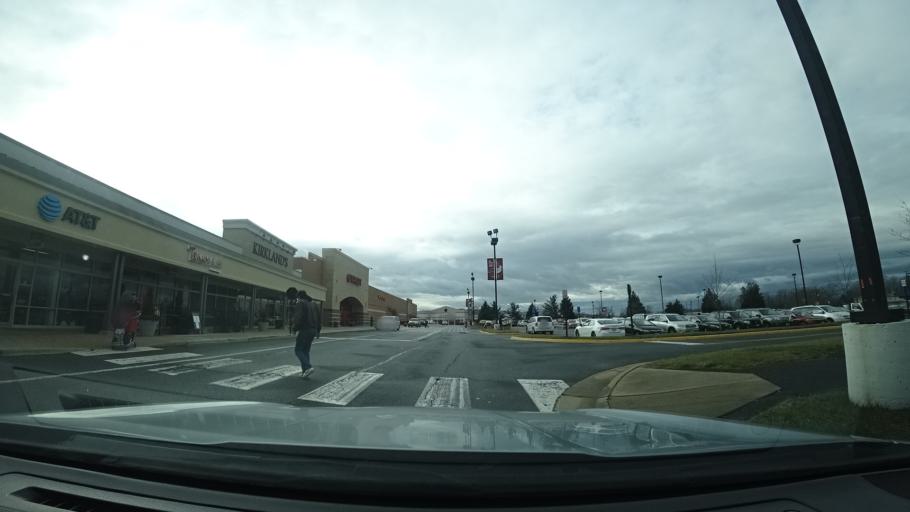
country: US
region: Virginia
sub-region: Fairfax County
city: Greenbriar
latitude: 38.8563
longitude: -77.3924
